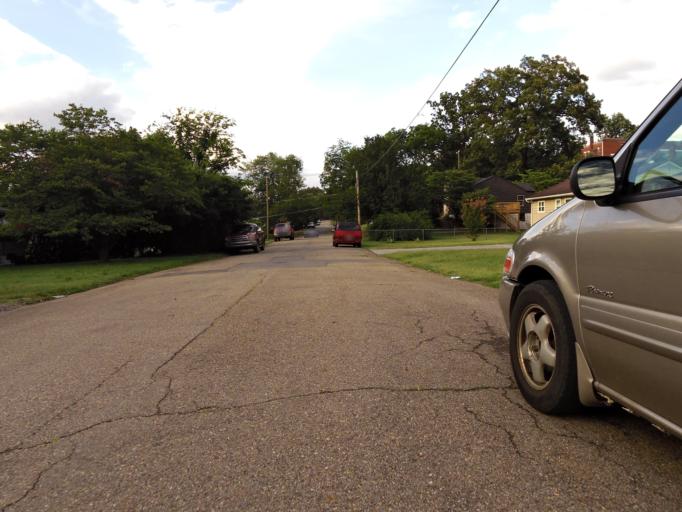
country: US
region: Tennessee
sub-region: Knox County
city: Knoxville
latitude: 35.9908
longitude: -83.9331
